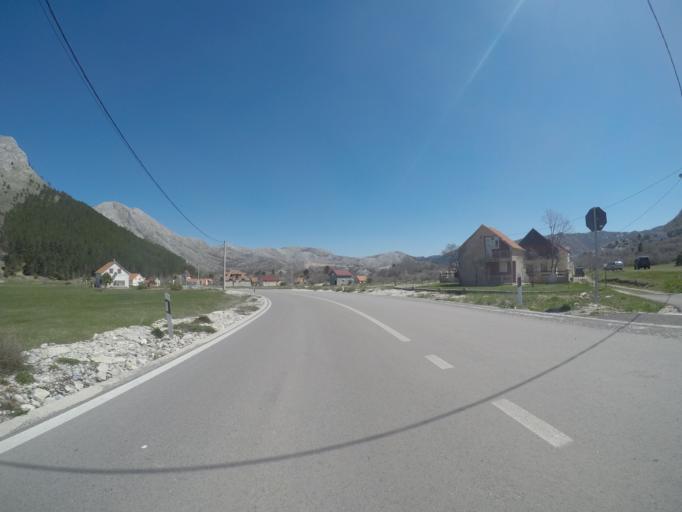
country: ME
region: Kotor
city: Kotor
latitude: 42.4270
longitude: 18.8037
